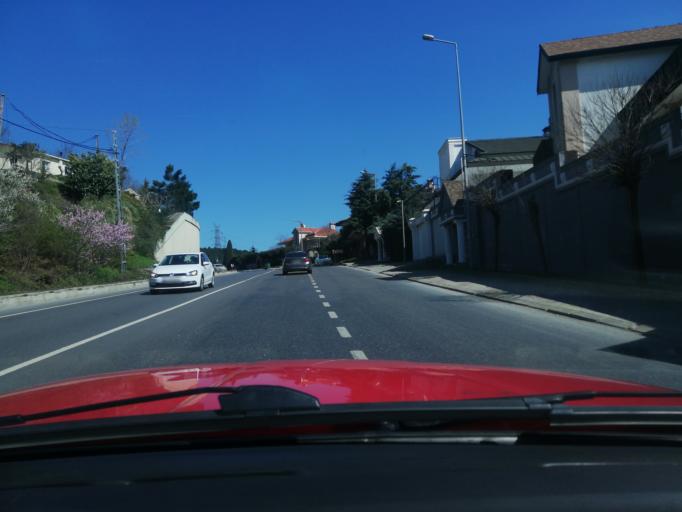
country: TR
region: Istanbul
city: Mahmut Sevket Pasa
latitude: 41.1212
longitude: 29.1380
